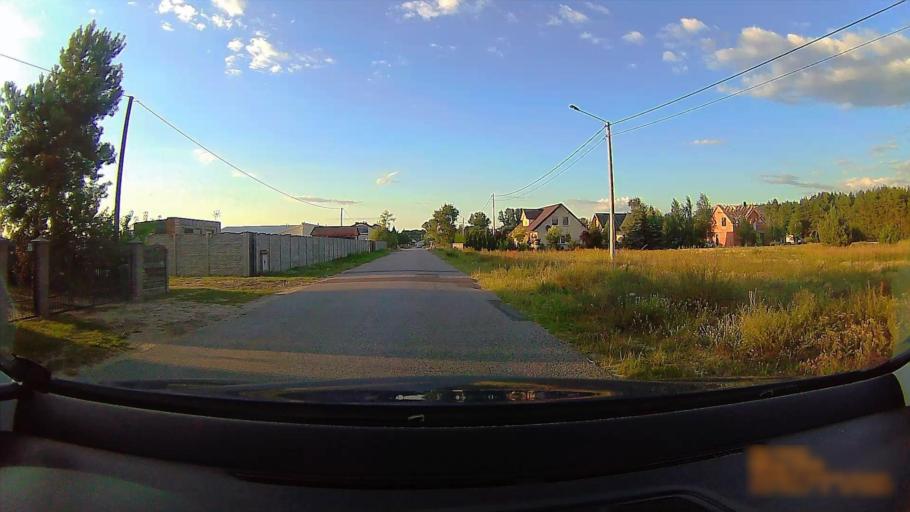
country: PL
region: Greater Poland Voivodeship
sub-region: Konin
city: Konin
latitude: 52.2117
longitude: 18.3248
